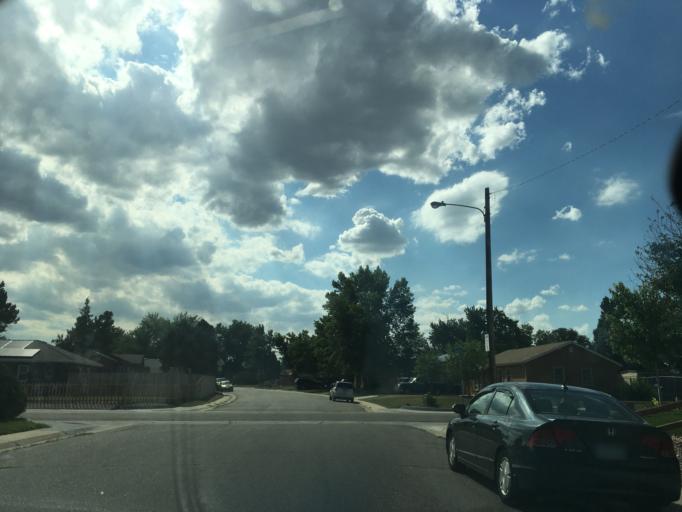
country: US
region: Colorado
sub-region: Arapahoe County
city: Sheridan
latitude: 39.6874
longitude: -105.0374
